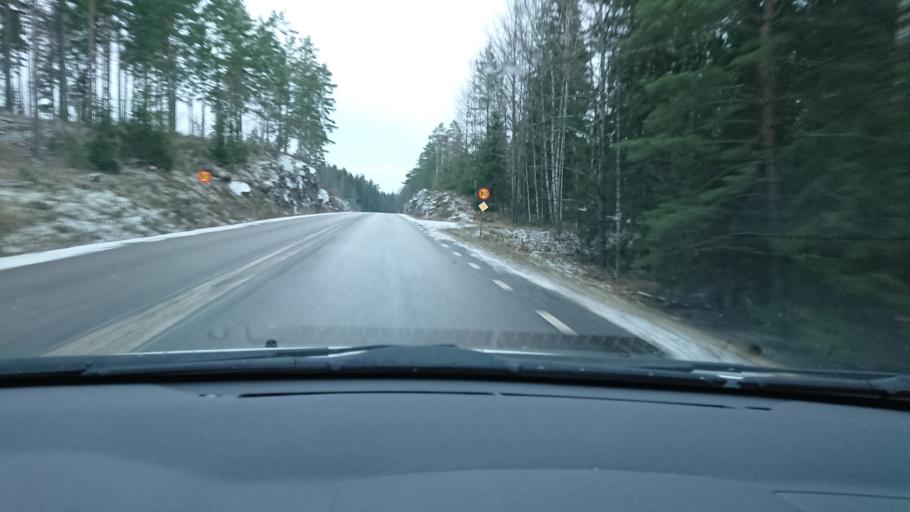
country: SE
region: Kalmar
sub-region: Hultsfreds Kommun
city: Hultsfred
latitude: 57.4906
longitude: 15.8249
